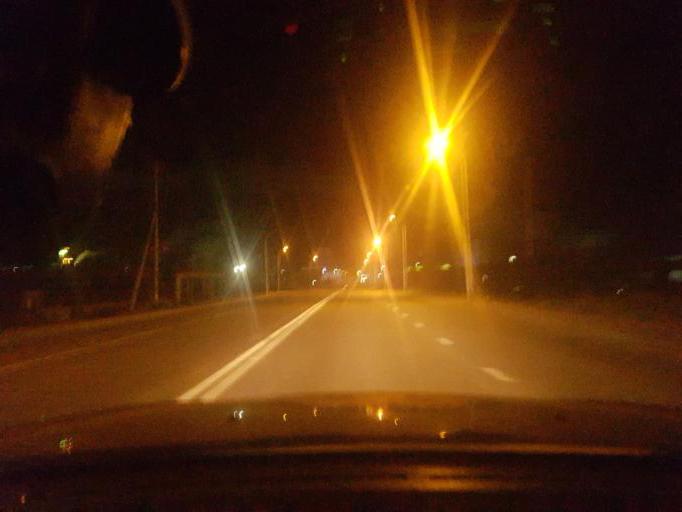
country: MN
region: Ulaanbaatar
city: Ulaanbaatar
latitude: 47.9032
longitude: 106.8721
